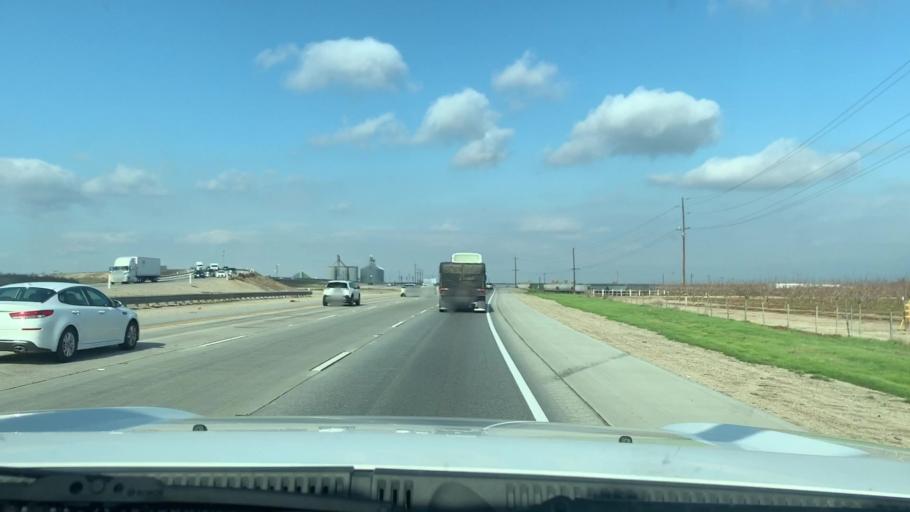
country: US
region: California
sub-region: Kern County
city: McFarland
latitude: 35.5863
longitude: -119.2041
